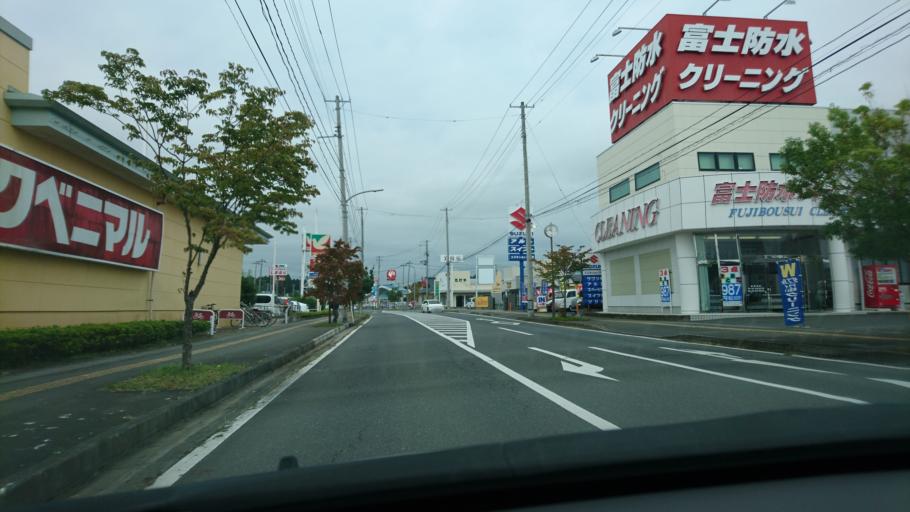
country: JP
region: Iwate
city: Ichinoseki
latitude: 38.7705
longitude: 141.1221
